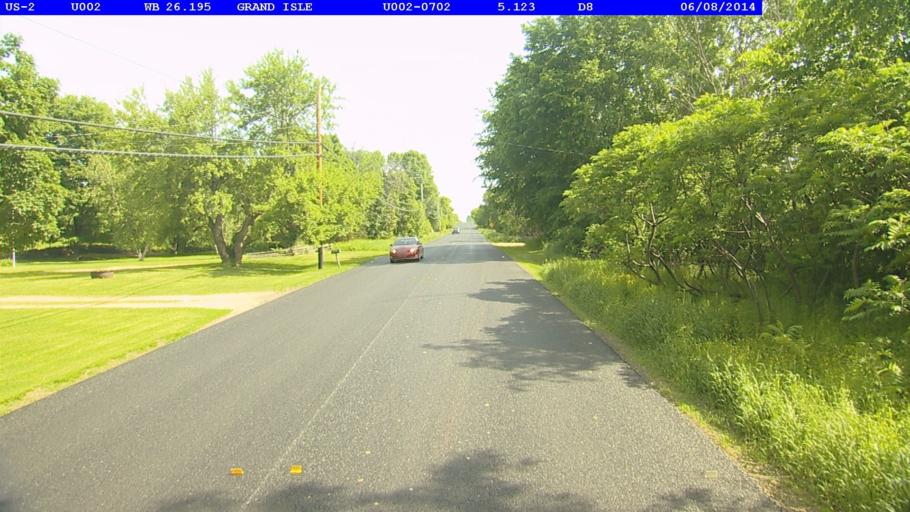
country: US
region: New York
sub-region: Clinton County
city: Cumberland Head
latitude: 44.6953
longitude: -73.3062
